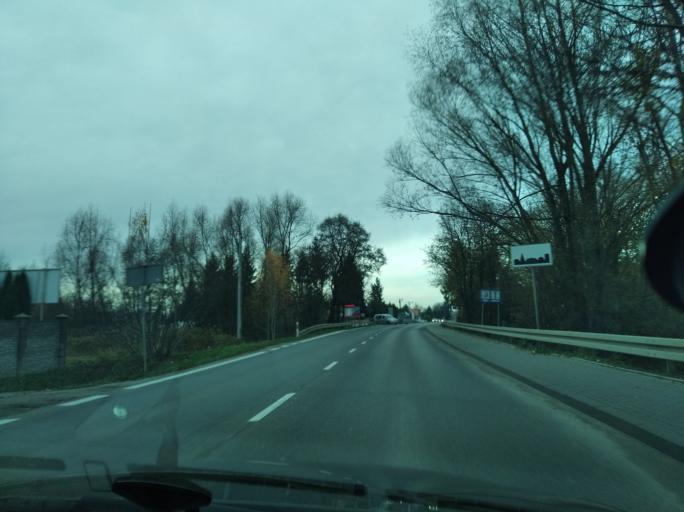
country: PL
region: Subcarpathian Voivodeship
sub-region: Powiat lancucki
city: Lancut
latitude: 50.0944
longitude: 22.2312
